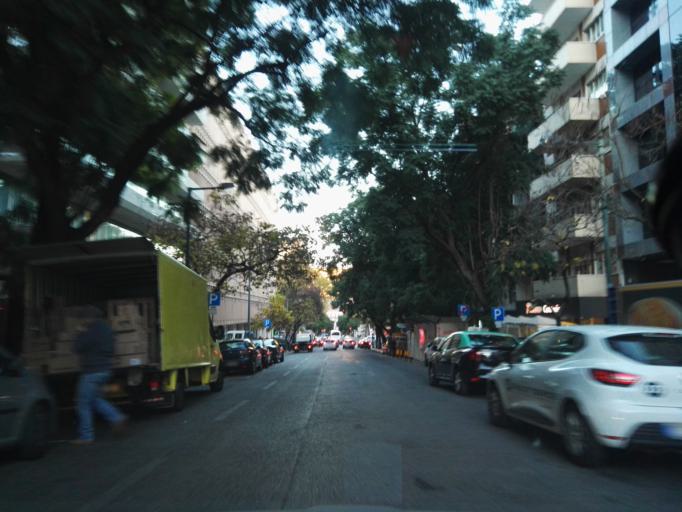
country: PT
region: Lisbon
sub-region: Lisbon
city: Lisbon
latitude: 38.7212
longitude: -9.1487
